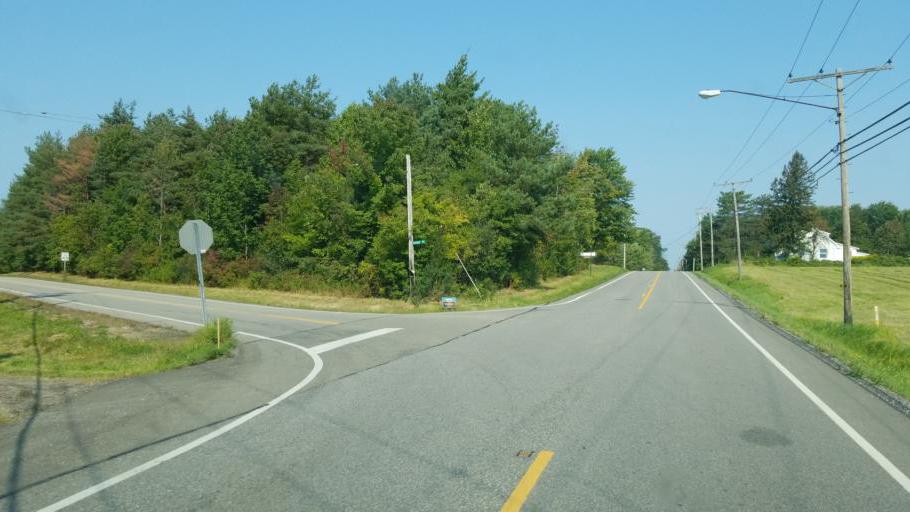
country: US
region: Ohio
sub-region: Geauga County
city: Chardon
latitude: 41.6067
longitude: -81.1486
